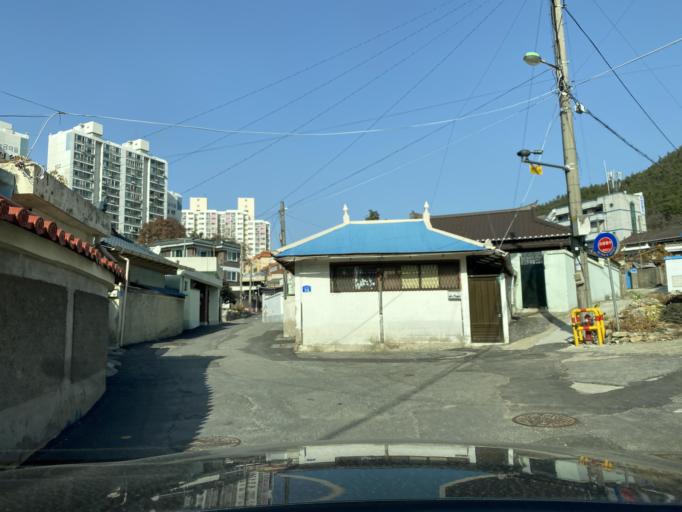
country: KR
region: Chungcheongnam-do
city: Yesan
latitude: 36.6839
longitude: 126.8462
